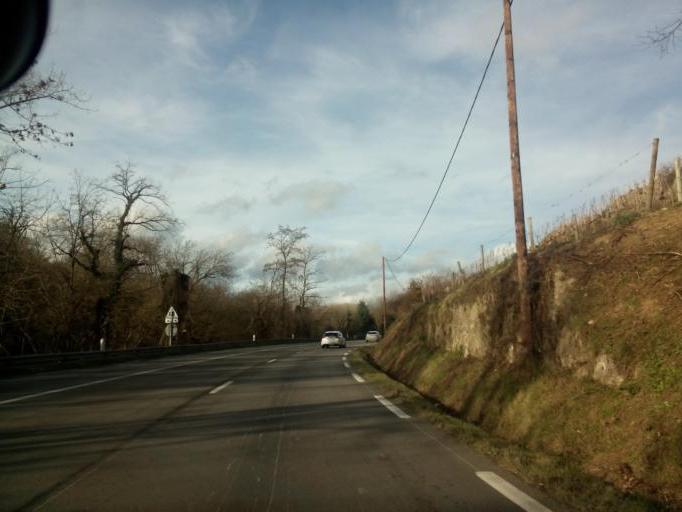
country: FR
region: Rhone-Alpes
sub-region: Departement de l'Ardeche
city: Serrieres
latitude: 45.3088
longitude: 4.7519
